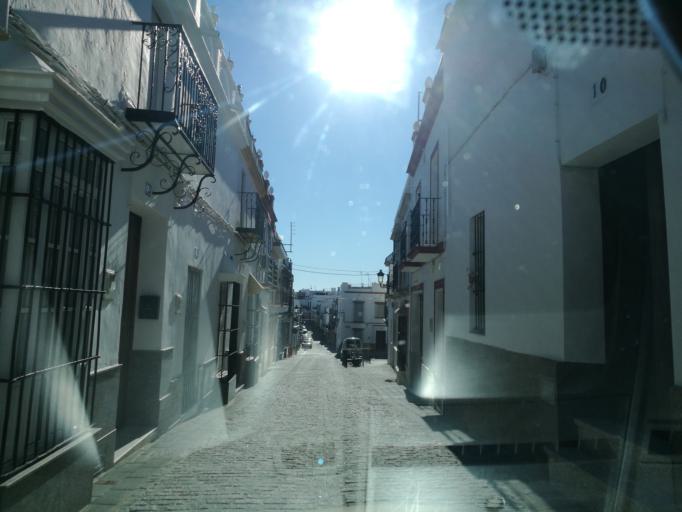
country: ES
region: Andalusia
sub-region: Provincia de Sevilla
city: La Campana
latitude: 37.5695
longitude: -5.4260
